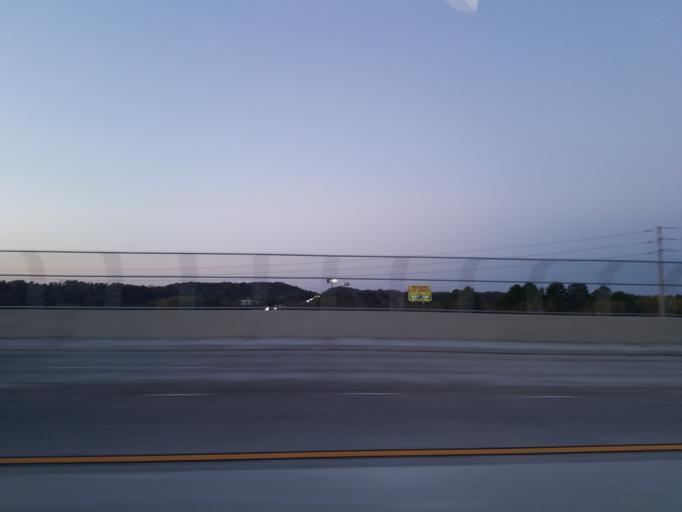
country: US
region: Georgia
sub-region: Gordon County
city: Calhoun
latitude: 34.5770
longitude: -84.9504
